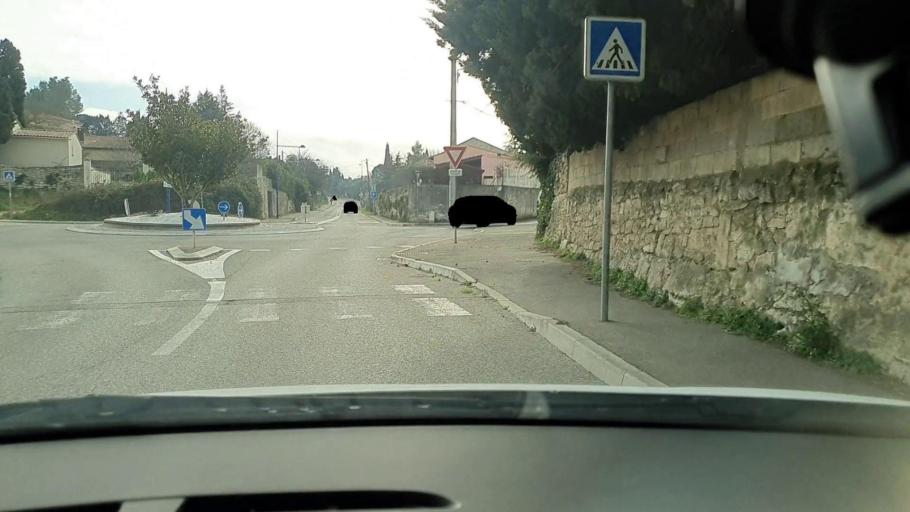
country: FR
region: Languedoc-Roussillon
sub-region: Departement du Gard
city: Beaucaire
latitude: 43.8166
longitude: 4.6301
